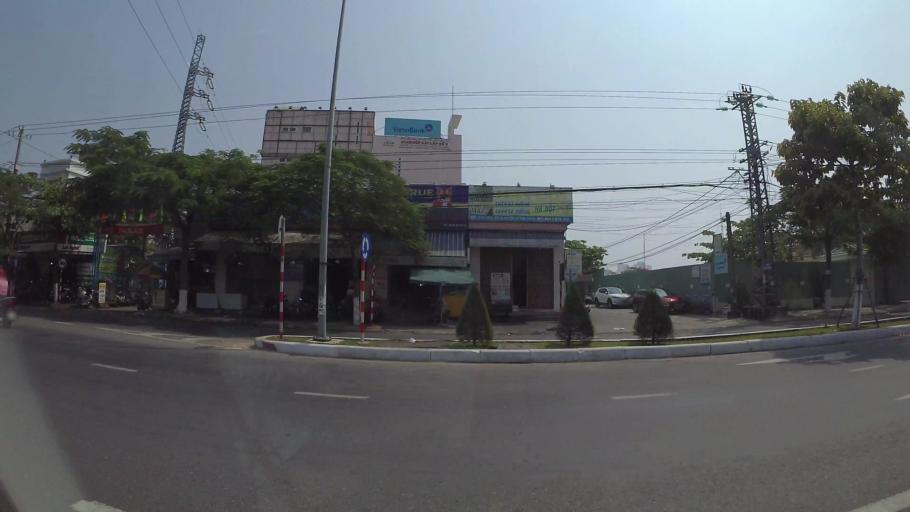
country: VN
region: Da Nang
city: Son Tra
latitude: 16.0523
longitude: 108.2372
